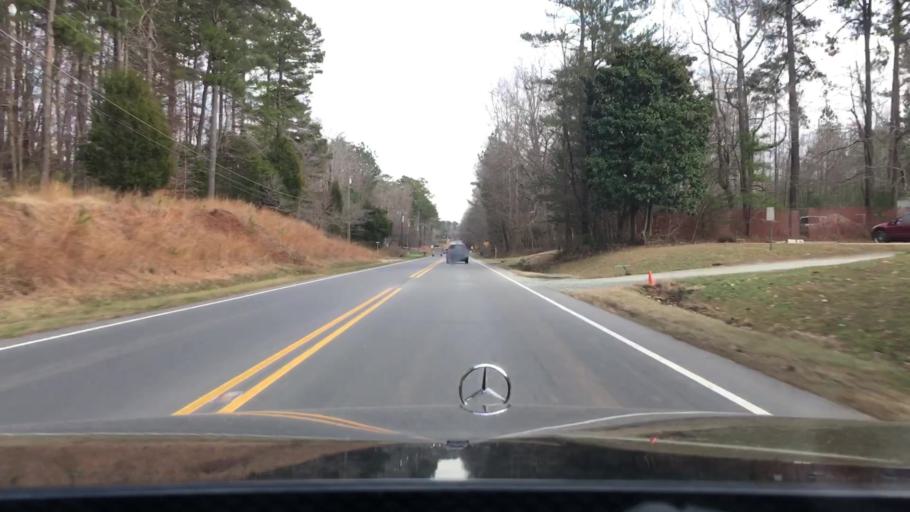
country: US
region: North Carolina
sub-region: Orange County
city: Hillsborough
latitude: 36.0482
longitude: -79.0274
